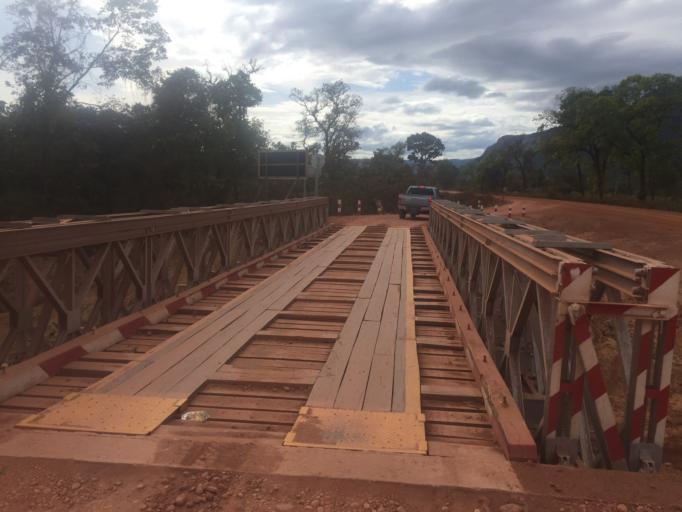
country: LA
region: Attapu
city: Attapu
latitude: 14.7672
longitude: 106.7299
